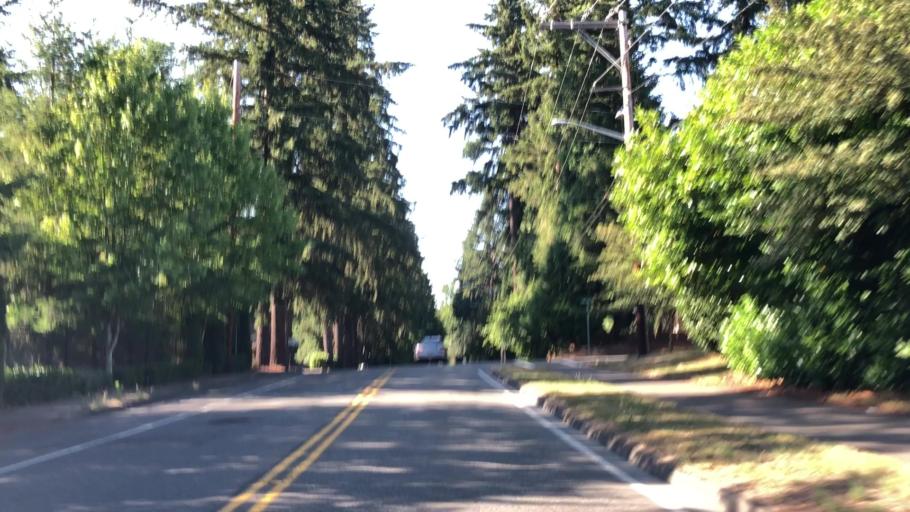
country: US
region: Washington
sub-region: King County
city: Woodinville
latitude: 47.7622
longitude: -122.1636
